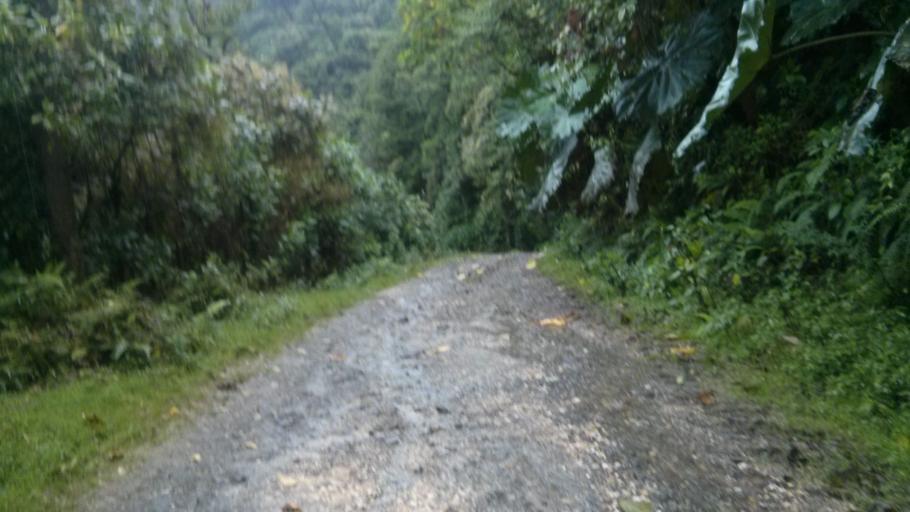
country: CR
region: San Jose
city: Ipis
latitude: 10.0317
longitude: -83.9406
